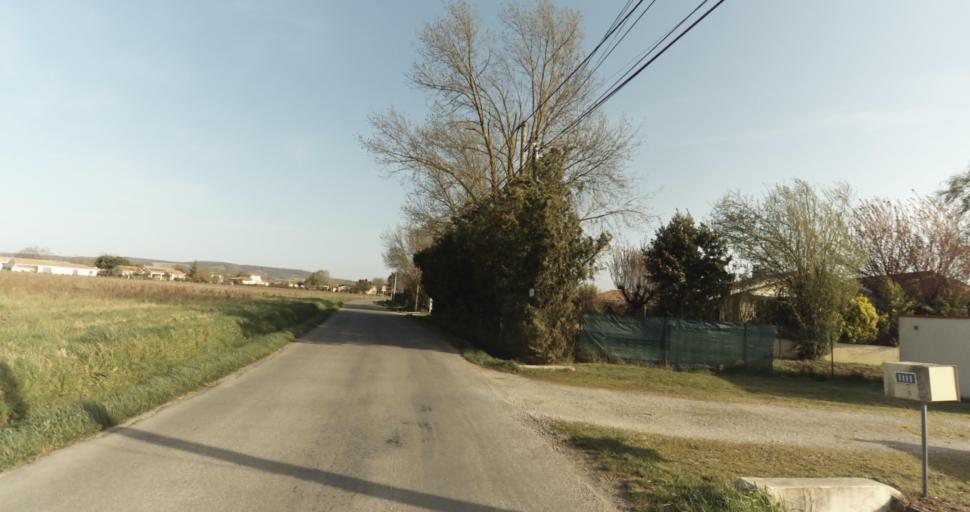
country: FR
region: Midi-Pyrenees
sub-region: Departement du Tarn
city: Saint-Sulpice-la-Pointe
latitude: 43.7620
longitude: 1.6778
